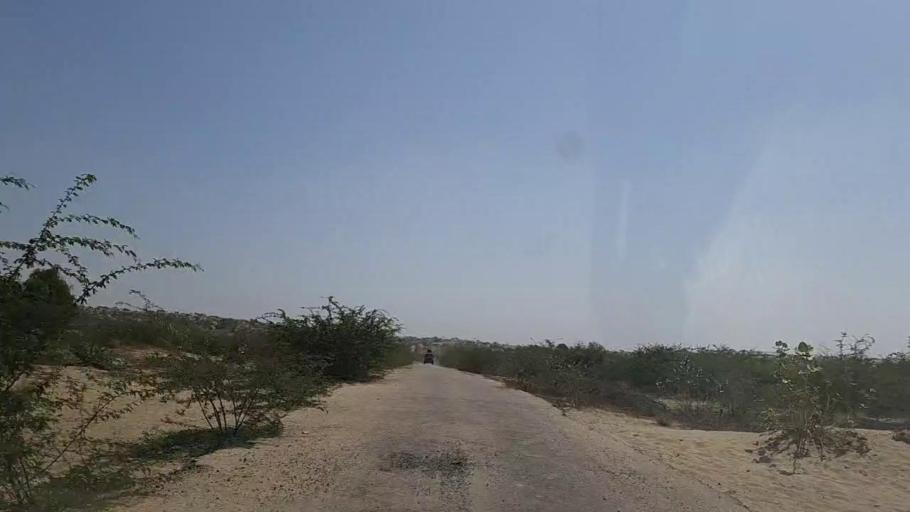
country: PK
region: Sindh
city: Diplo
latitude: 24.4943
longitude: 69.4335
